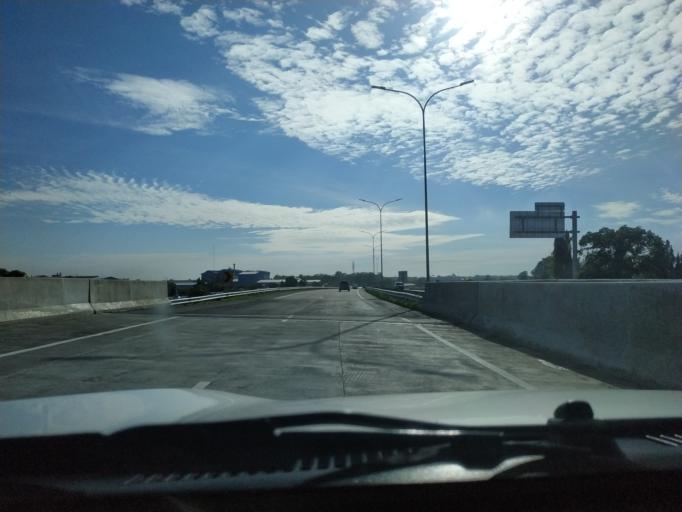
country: ID
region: North Sumatra
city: Deli Tua
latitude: 3.5335
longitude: 98.7816
